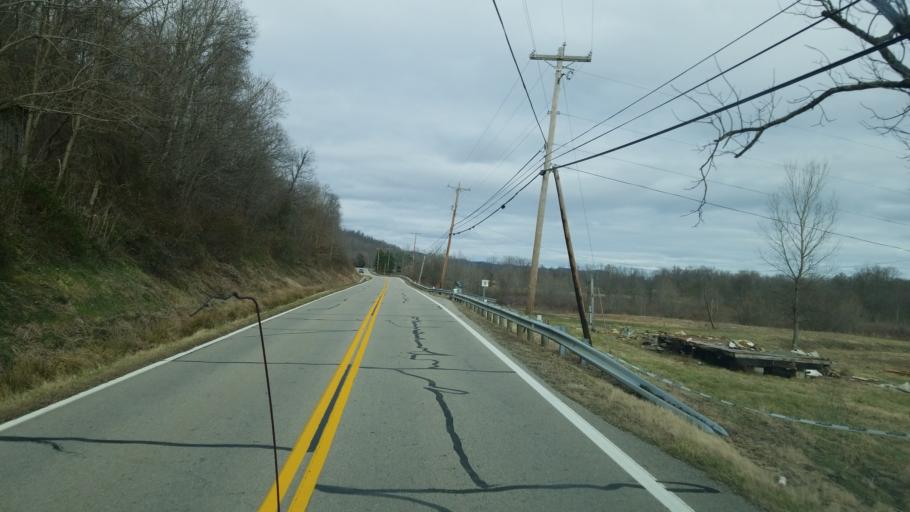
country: US
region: Ohio
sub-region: Scioto County
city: West Portsmouth
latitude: 38.6528
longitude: -83.1332
